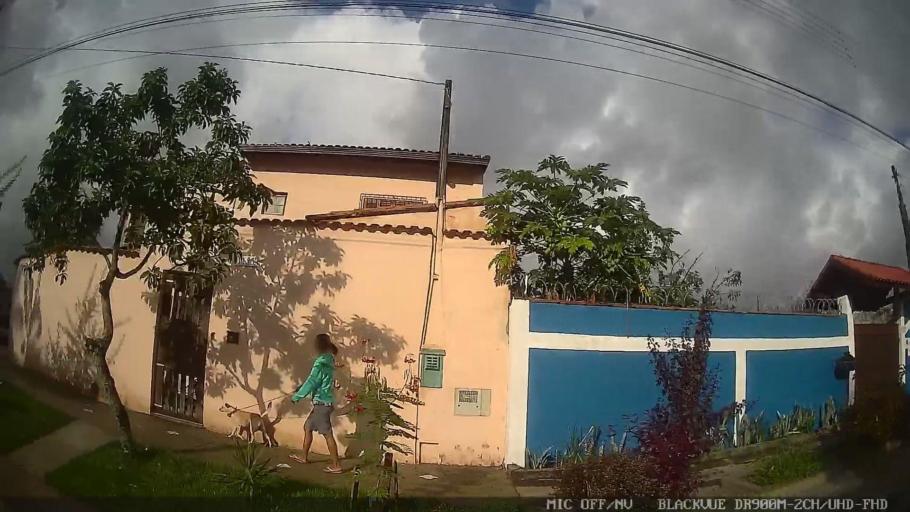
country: BR
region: Sao Paulo
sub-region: Itanhaem
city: Itanhaem
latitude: -24.1956
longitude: -46.8666
